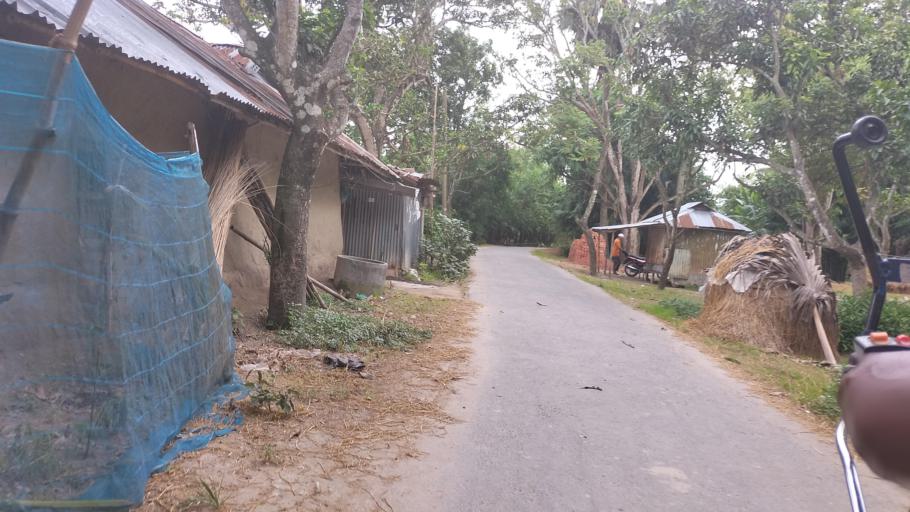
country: BD
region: Rajshahi
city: Rajshahi
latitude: 24.5499
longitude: 88.6048
